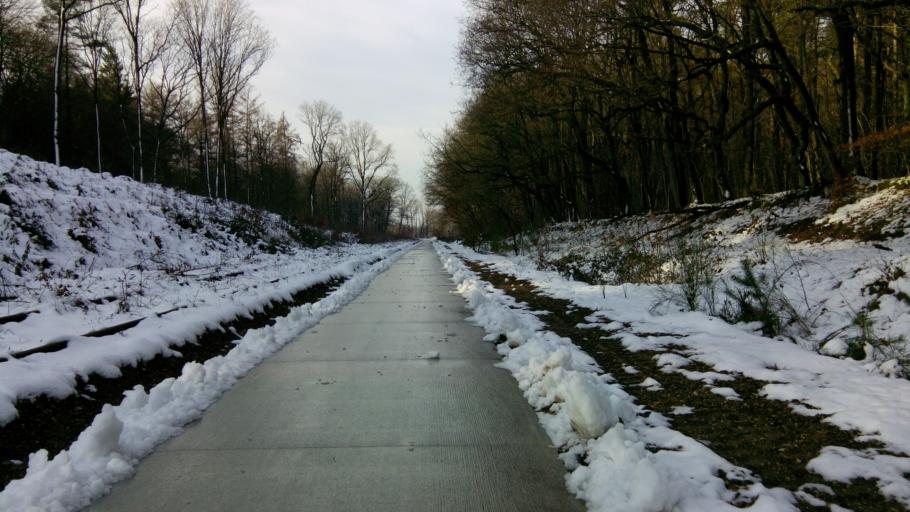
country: NL
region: Gelderland
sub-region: Gemeente Groesbeek
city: Groesbeek
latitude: 51.7761
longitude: 5.8987
